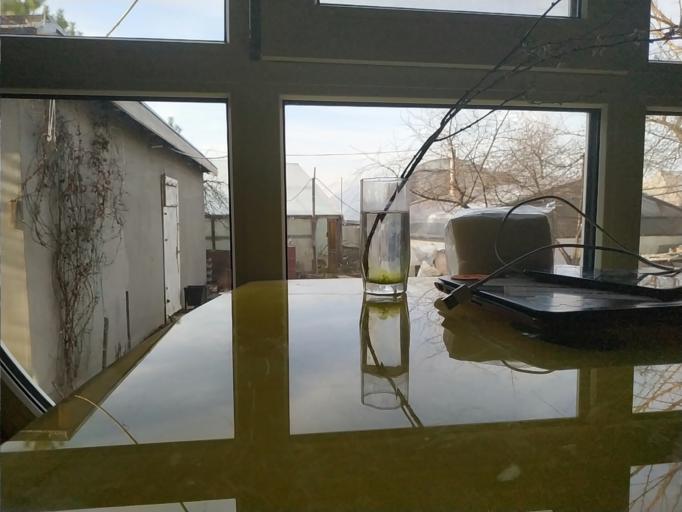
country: RU
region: Republic of Karelia
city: Suoyarvi
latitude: 61.7599
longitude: 32.3194
